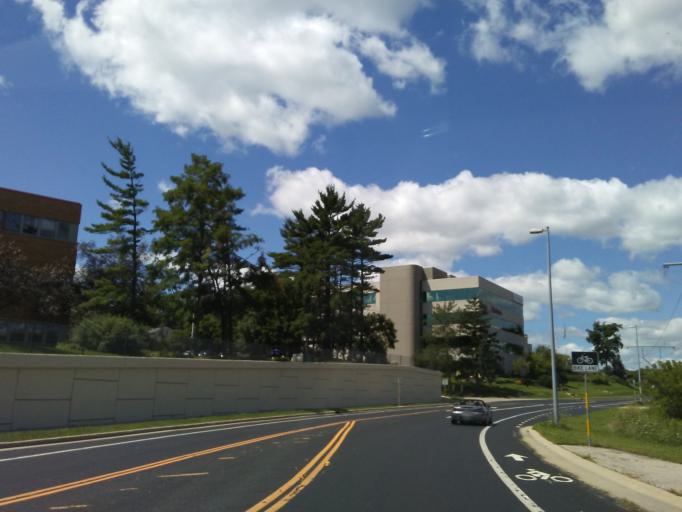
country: US
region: Wisconsin
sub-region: Dane County
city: Shorewood Hills
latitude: 43.0348
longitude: -89.4275
